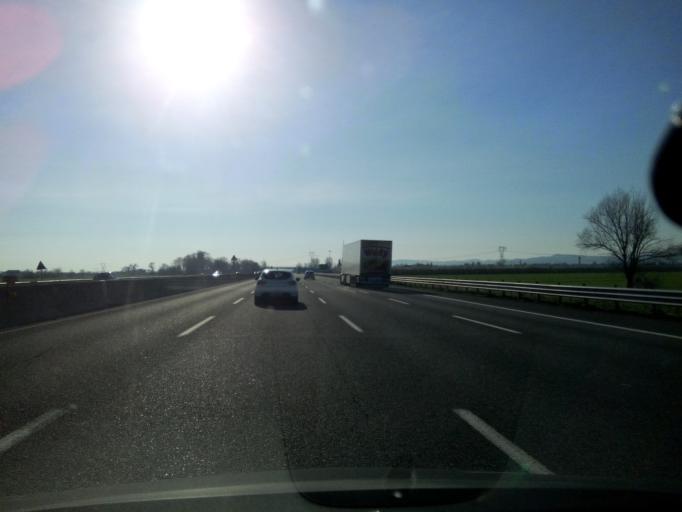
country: IT
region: Emilia-Romagna
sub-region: Provincia di Modena
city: San Cesario sul Panaro
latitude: 44.5616
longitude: 11.0521
